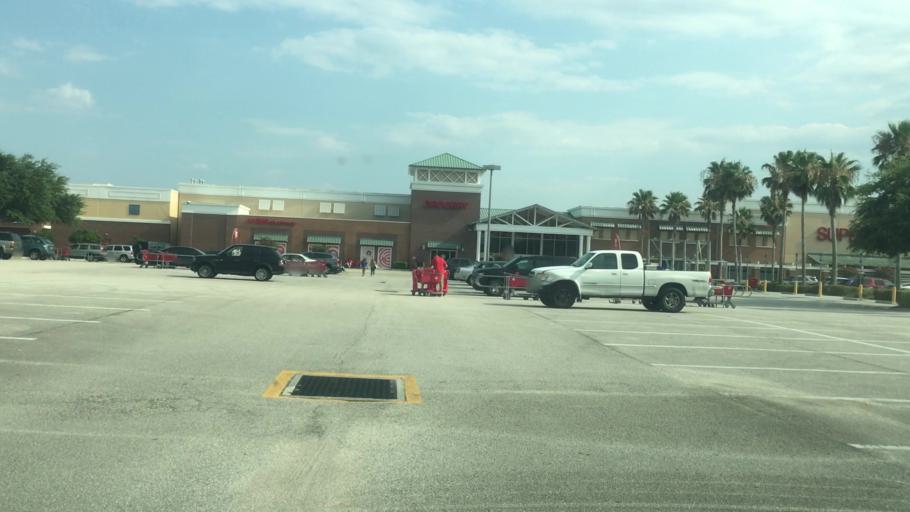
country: US
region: Florida
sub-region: Duval County
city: Jacksonville Beach
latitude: 30.2863
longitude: -81.4561
